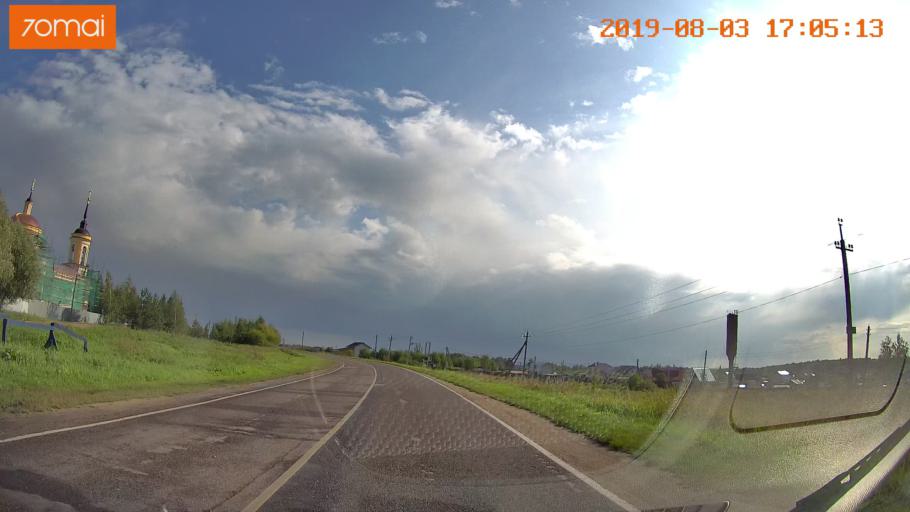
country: RU
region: Moskovskaya
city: Troitskoye
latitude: 55.3232
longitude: 38.5522
